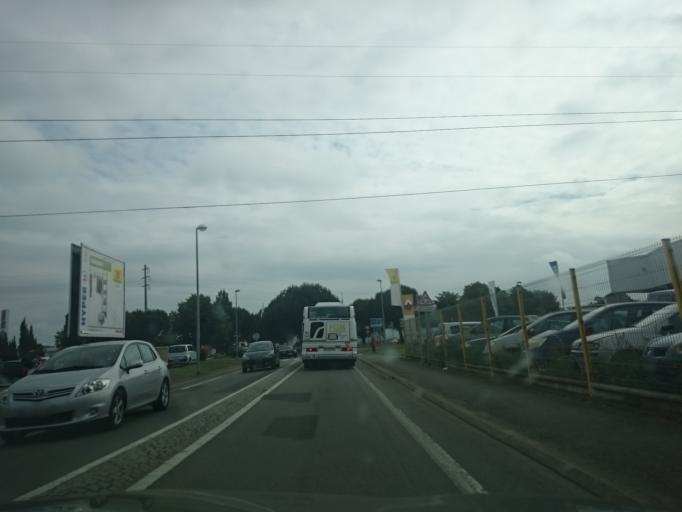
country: FR
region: Pays de la Loire
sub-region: Departement de la Loire-Atlantique
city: La Montagne
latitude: 47.1773
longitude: -1.6790
